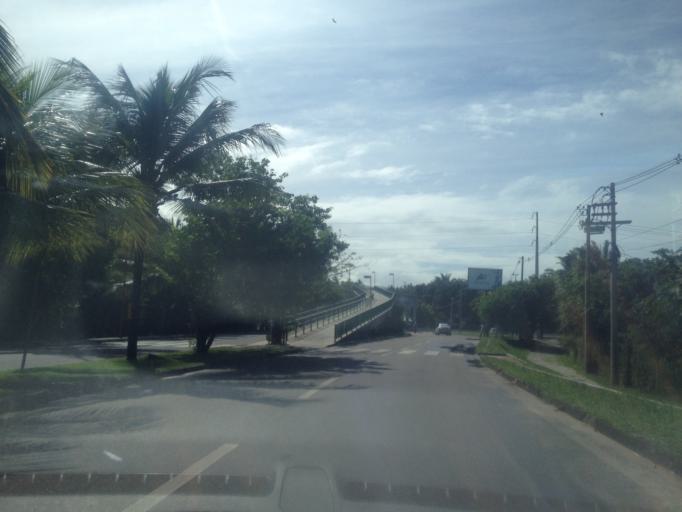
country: BR
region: Bahia
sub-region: Mata De Sao Joao
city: Mata de Sao Joao
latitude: -12.5643
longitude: -38.0173
